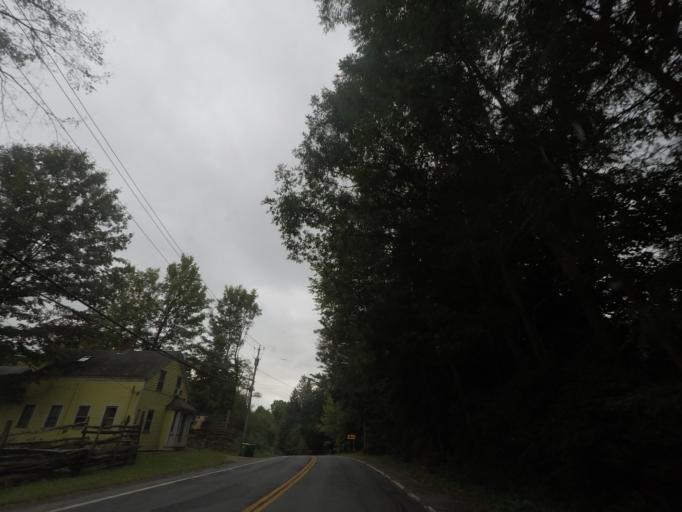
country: US
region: New York
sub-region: Rensselaer County
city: Hoosick Falls
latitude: 42.9123
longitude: -73.3522
